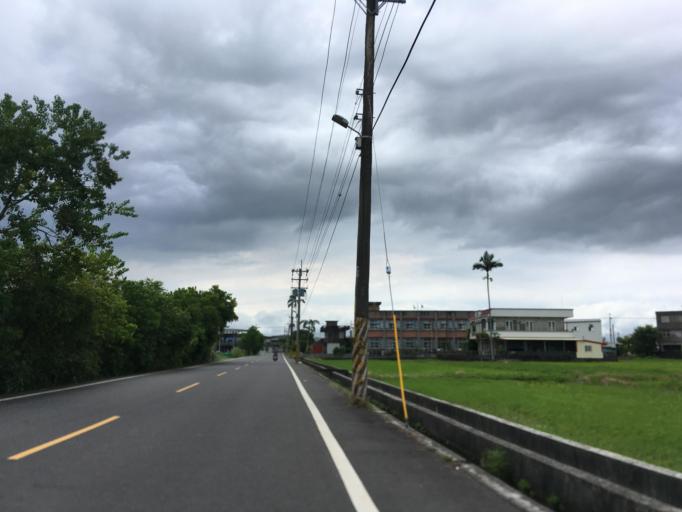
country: TW
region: Taiwan
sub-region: Yilan
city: Yilan
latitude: 24.6878
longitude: 121.8057
